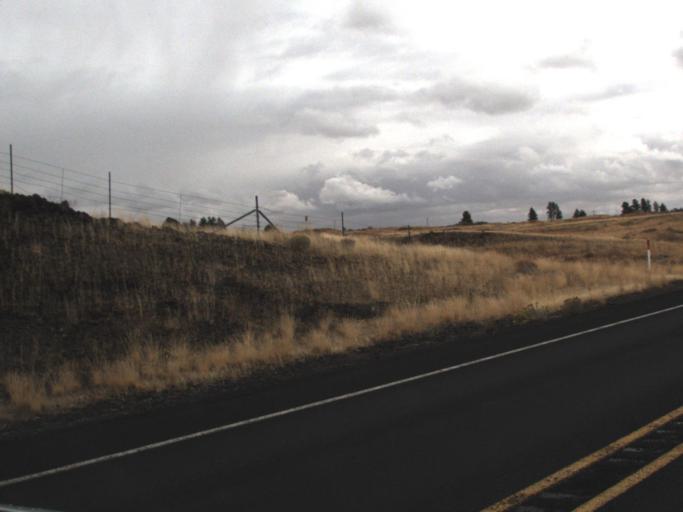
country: US
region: Washington
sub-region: Lincoln County
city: Davenport
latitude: 47.7001
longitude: -118.4064
